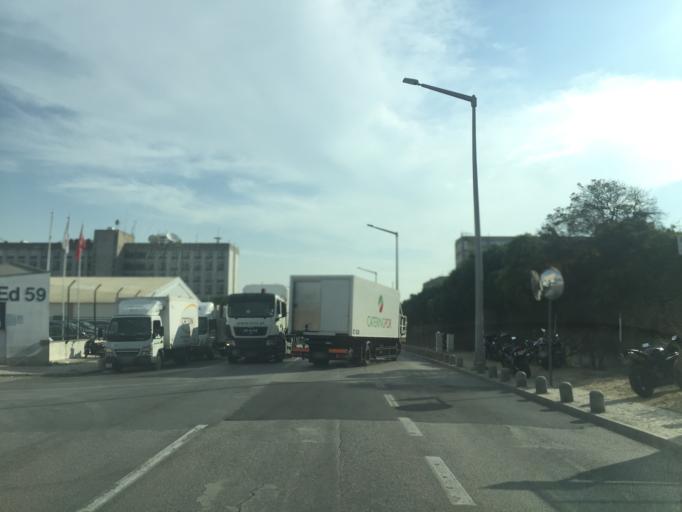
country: PT
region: Lisbon
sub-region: Loures
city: Sacavem
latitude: 38.7775
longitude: -9.1269
